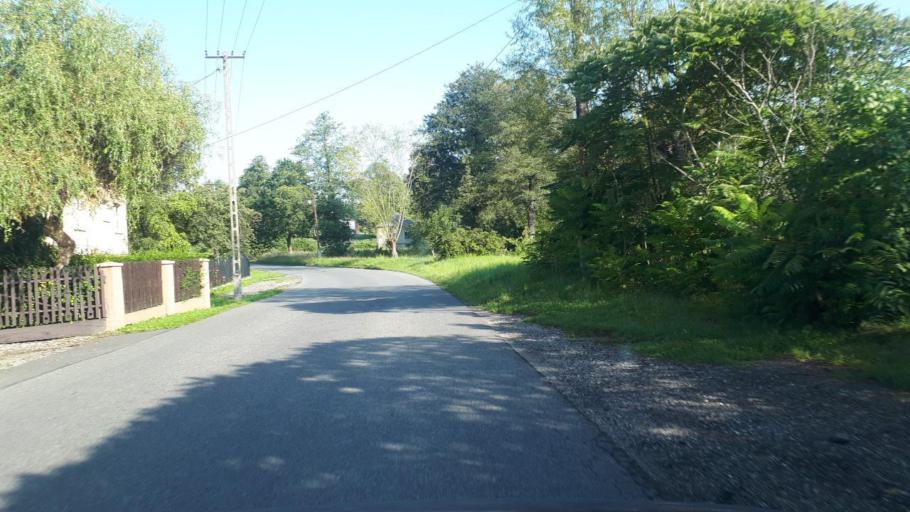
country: PL
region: Silesian Voivodeship
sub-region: Powiat cieszynski
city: Chybie
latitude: 49.8670
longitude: 18.8588
